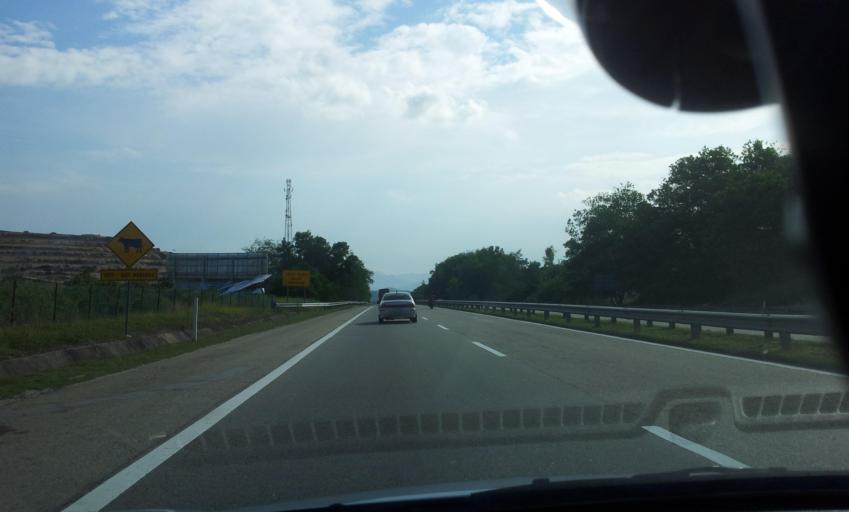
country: MY
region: Pahang
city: Bentong Town
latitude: 3.5094
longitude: 102.1236
